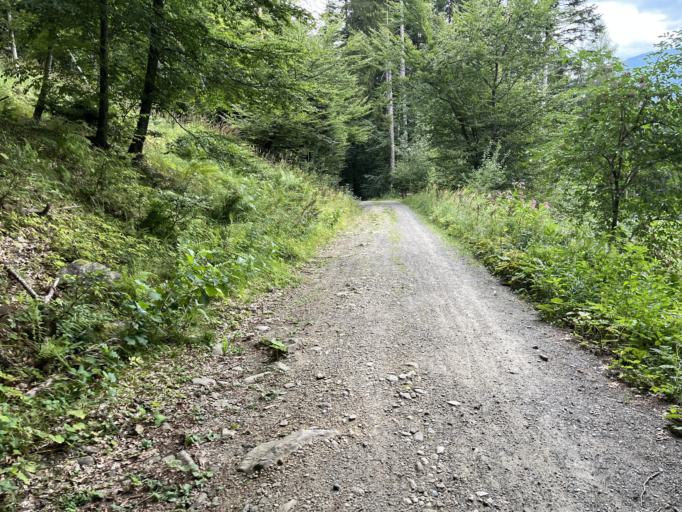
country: AT
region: Carinthia
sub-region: Politischer Bezirk Spittal an der Drau
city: Seeboden
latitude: 46.7999
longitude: 13.5406
